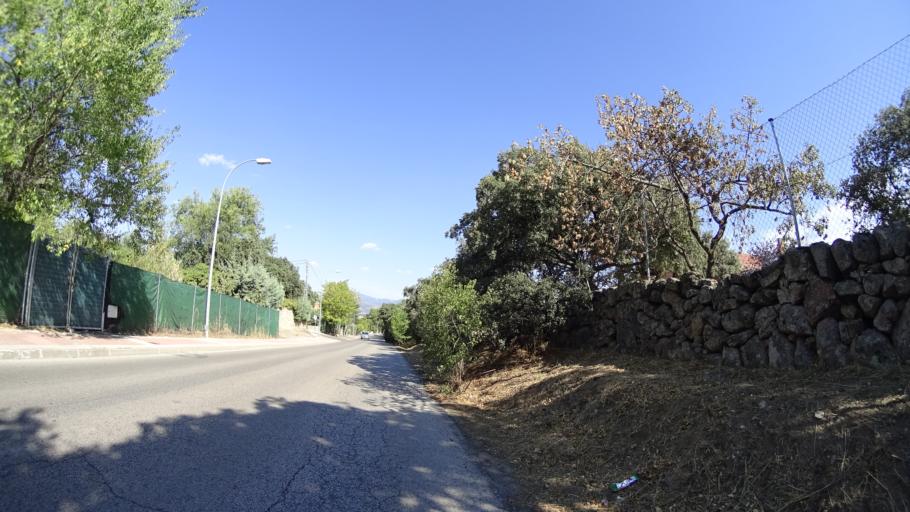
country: ES
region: Madrid
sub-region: Provincia de Madrid
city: Collado-Villalba
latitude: 40.6179
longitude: -4.0061
